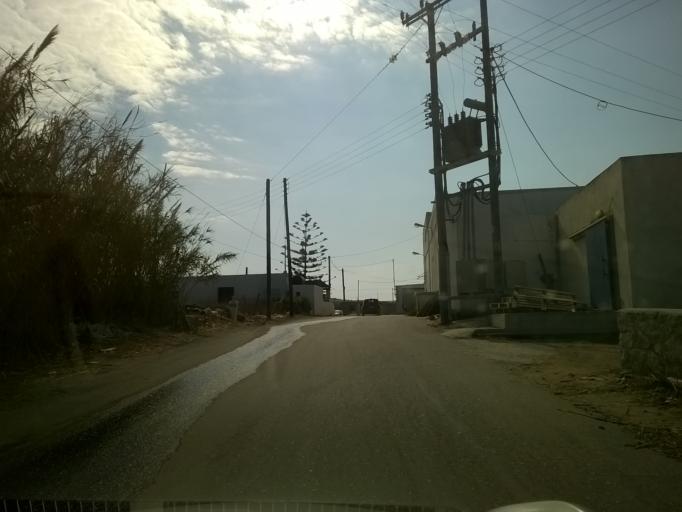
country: GR
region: South Aegean
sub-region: Nomos Kykladon
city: Naxos
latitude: 37.0733
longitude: 25.3859
